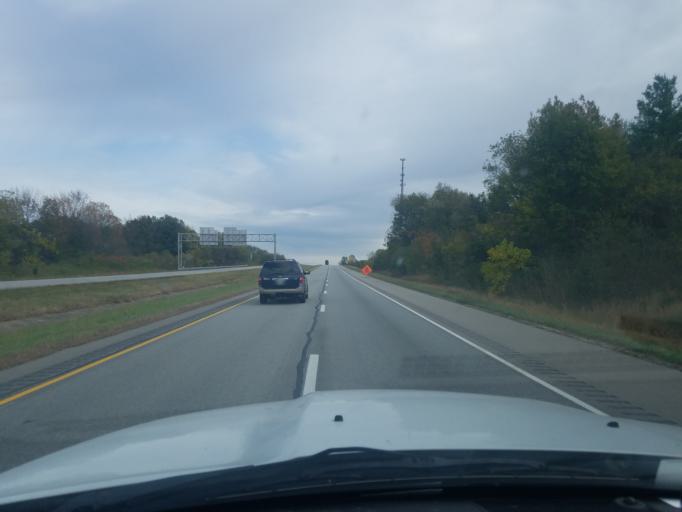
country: US
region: Indiana
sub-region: Gibson County
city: Haubstadt
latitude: 38.1696
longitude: -87.4458
